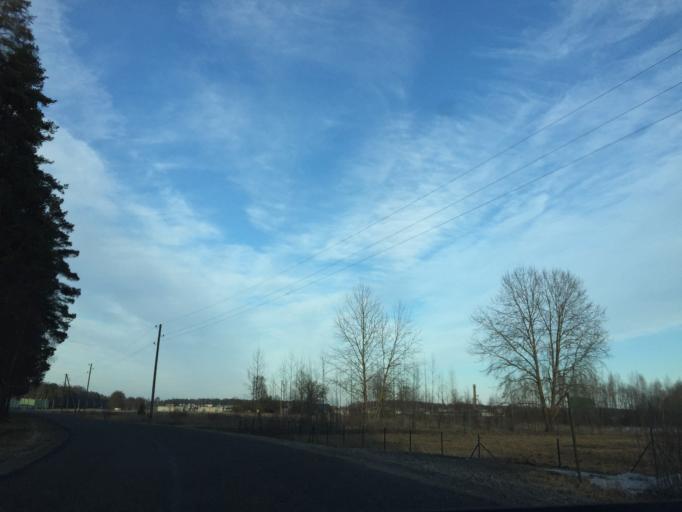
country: LV
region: Kekava
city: Kekava
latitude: 56.8209
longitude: 24.1873
